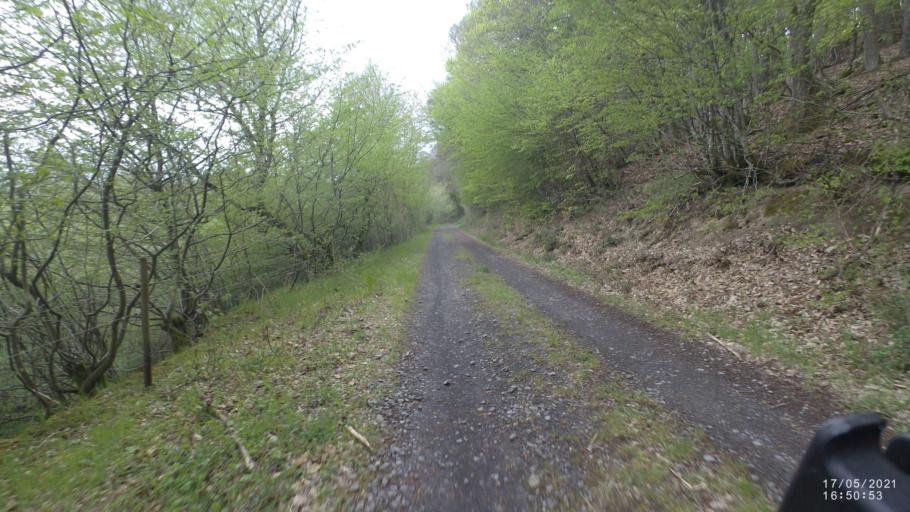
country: DE
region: Rheinland-Pfalz
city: Lind
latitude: 50.3134
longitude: 7.0416
